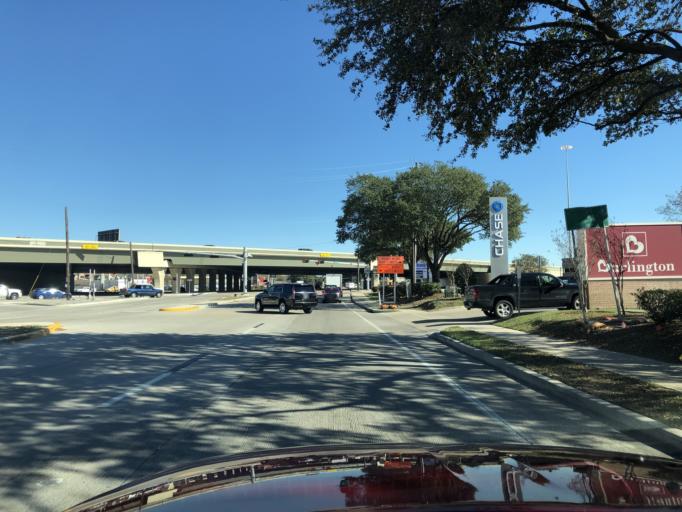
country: US
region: Texas
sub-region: Harris County
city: Spring Valley
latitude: 29.8332
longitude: -95.4853
